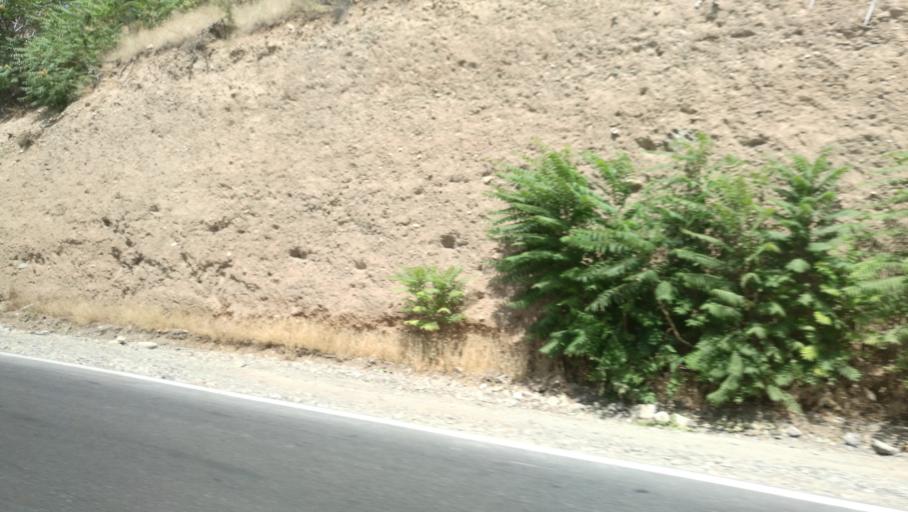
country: IR
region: Alborz
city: Karaj
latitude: 35.9306
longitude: 51.0608
